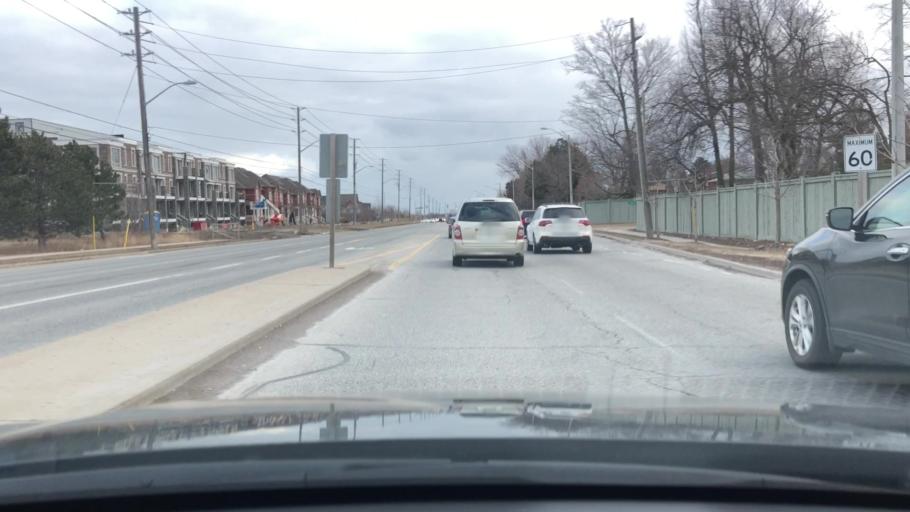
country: CA
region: Ontario
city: Markham
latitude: 43.8785
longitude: -79.2348
